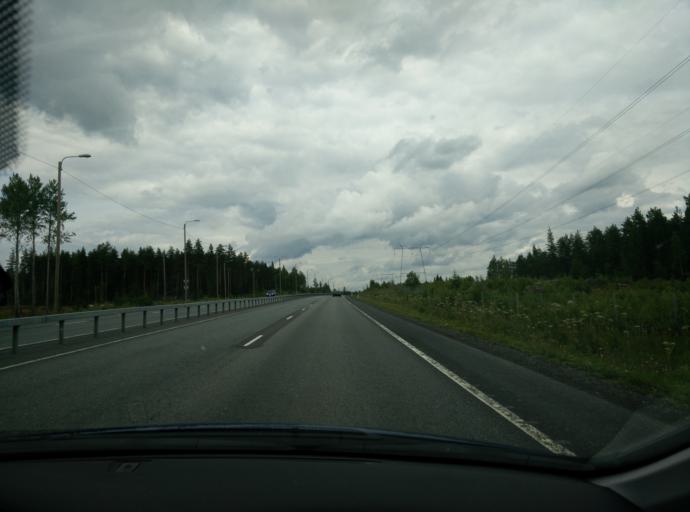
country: FI
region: Pirkanmaa
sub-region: Tampere
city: Kangasala
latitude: 61.6137
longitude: 24.1498
